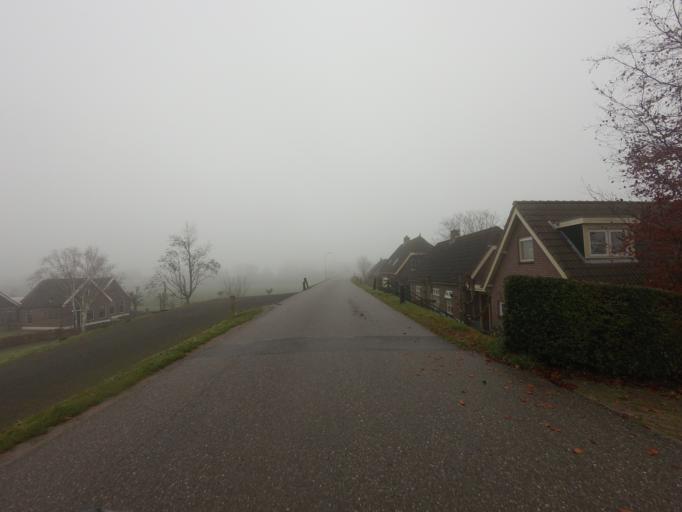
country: NL
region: Gelderland
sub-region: Gemeente Zaltbommel
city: Nederhemert
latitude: 51.7636
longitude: 5.1519
